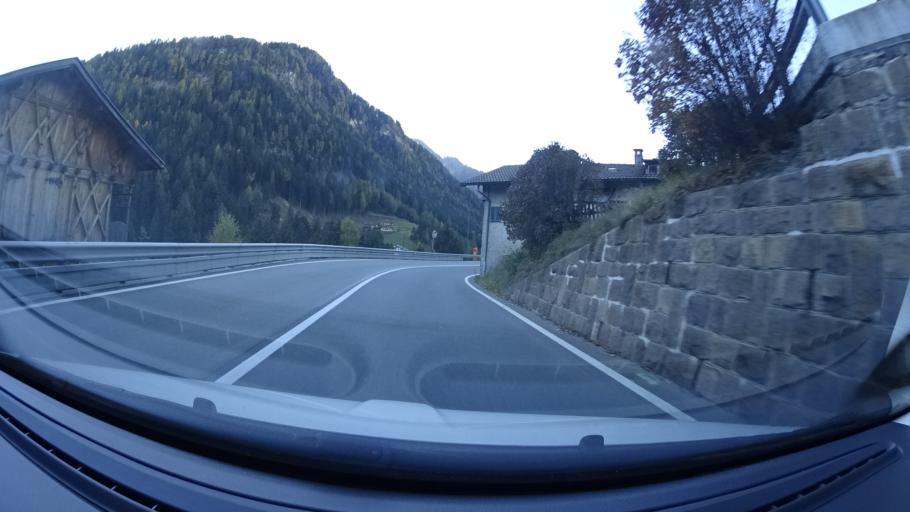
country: IT
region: Trentino-Alto Adige
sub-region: Bolzano
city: Santa Cristina Valgardena
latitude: 46.5614
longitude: 11.7046
